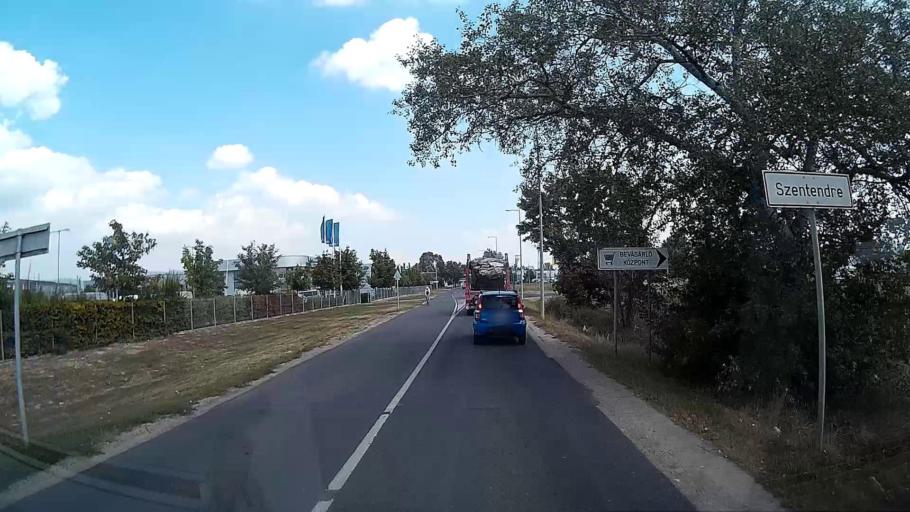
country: HU
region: Pest
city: Budakalasz
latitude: 47.6397
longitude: 19.0655
